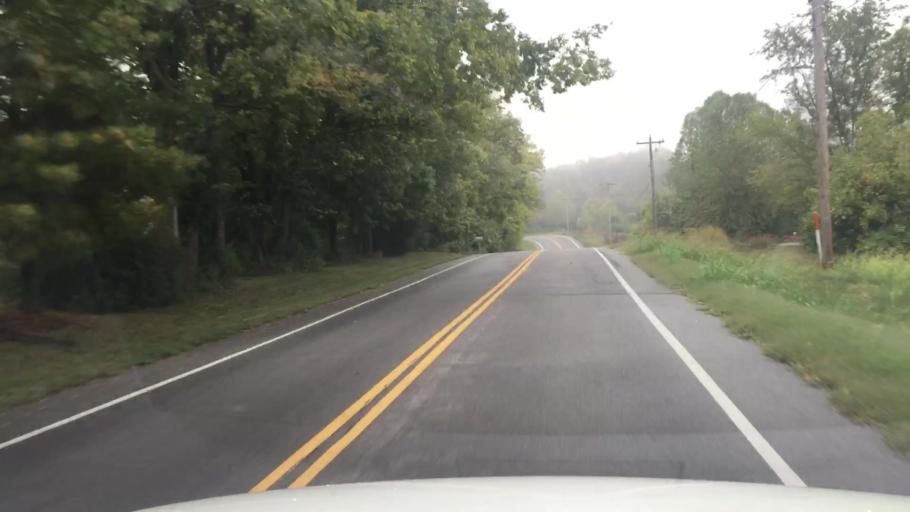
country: US
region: Missouri
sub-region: Boone County
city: Columbia
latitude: 38.8721
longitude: -92.4109
